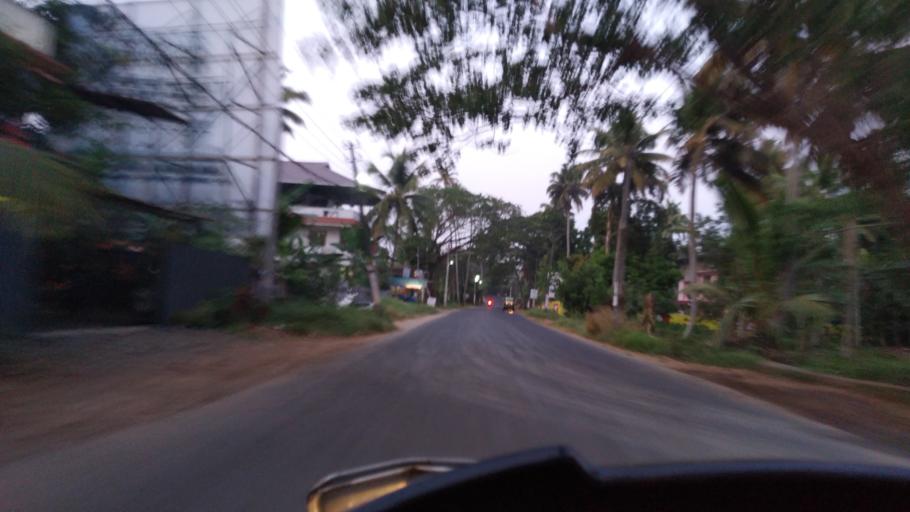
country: IN
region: Kerala
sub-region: Kottayam
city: Kottayam
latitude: 9.6085
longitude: 76.4336
